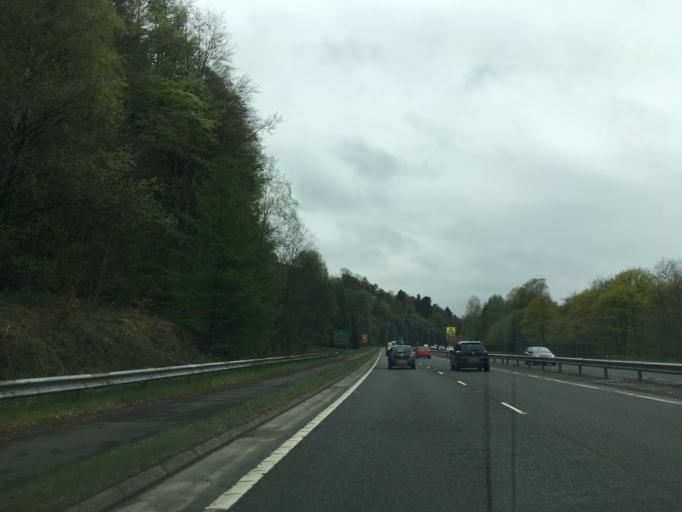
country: GB
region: Scotland
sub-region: Argyll and Bute
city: Cardross
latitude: 55.9303
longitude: -4.6342
